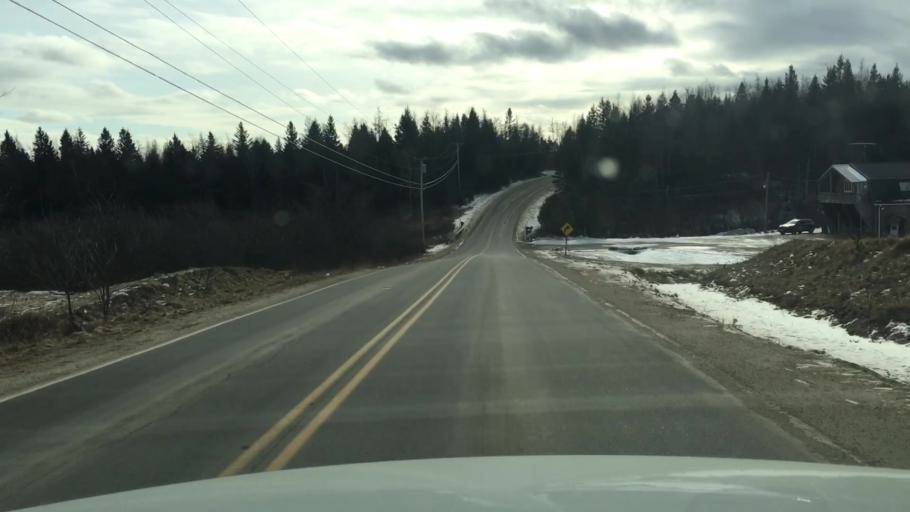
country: US
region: Maine
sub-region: Washington County
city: Jonesport
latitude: 44.6294
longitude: -67.5963
